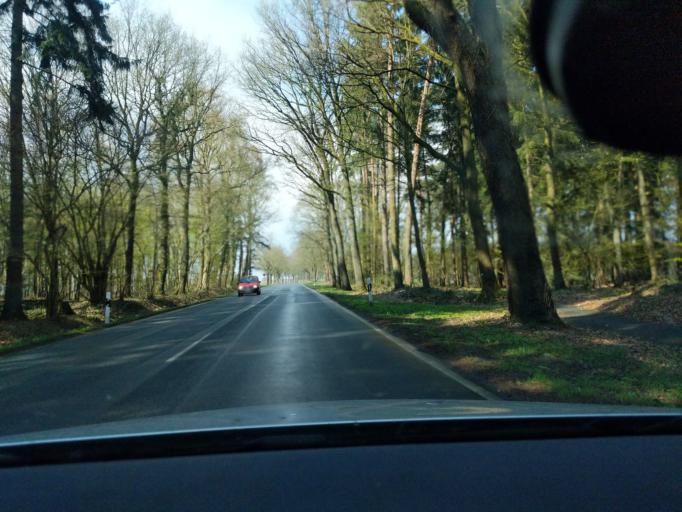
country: DE
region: Lower Saxony
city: Harsefeld
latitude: 53.4674
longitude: 9.4962
